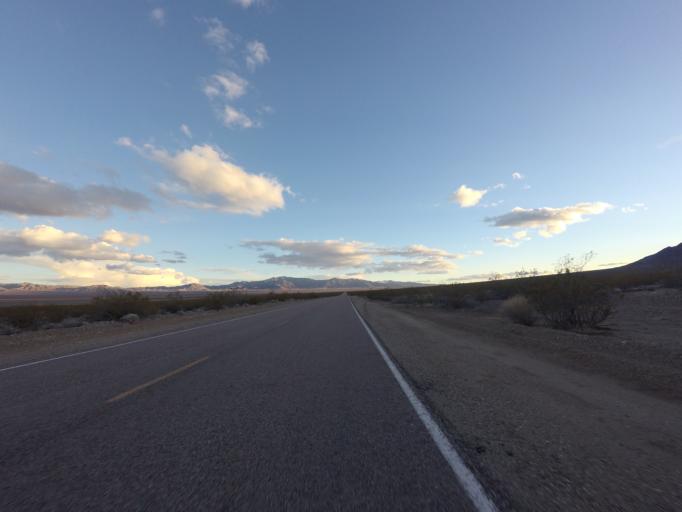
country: US
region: Nevada
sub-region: Clark County
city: Sandy Valley
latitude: 35.4464
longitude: -115.3881
